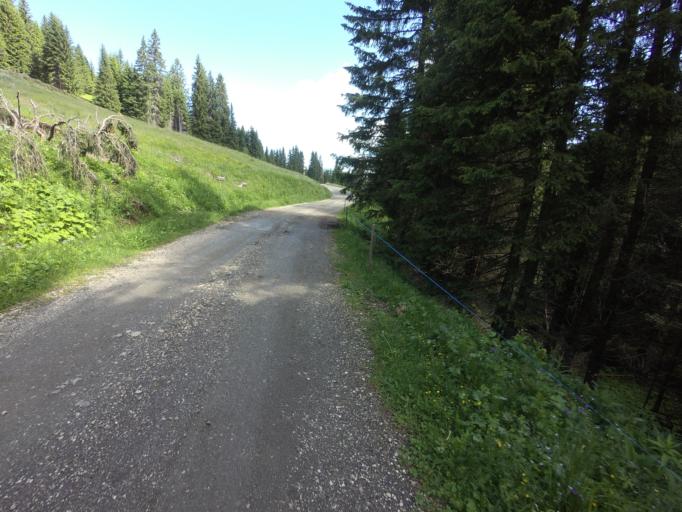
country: IT
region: Trentino-Alto Adige
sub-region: Bolzano
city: Ortisei
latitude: 46.5153
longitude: 11.6651
